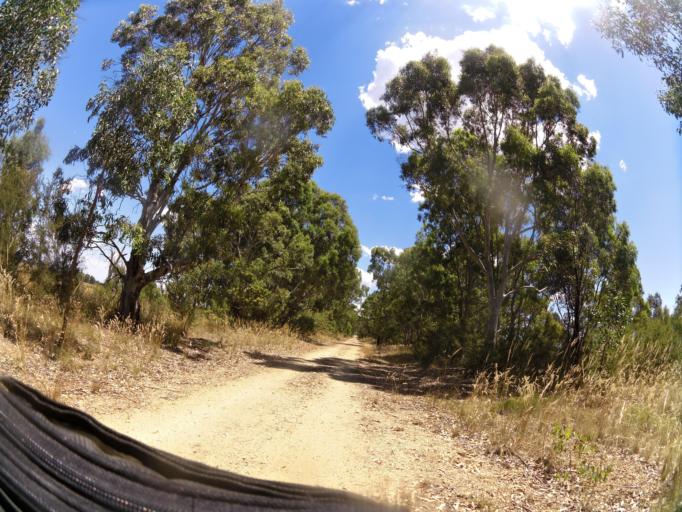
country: AU
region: Victoria
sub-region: Wellington
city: Heyfield
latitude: -37.9813
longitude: 146.8377
